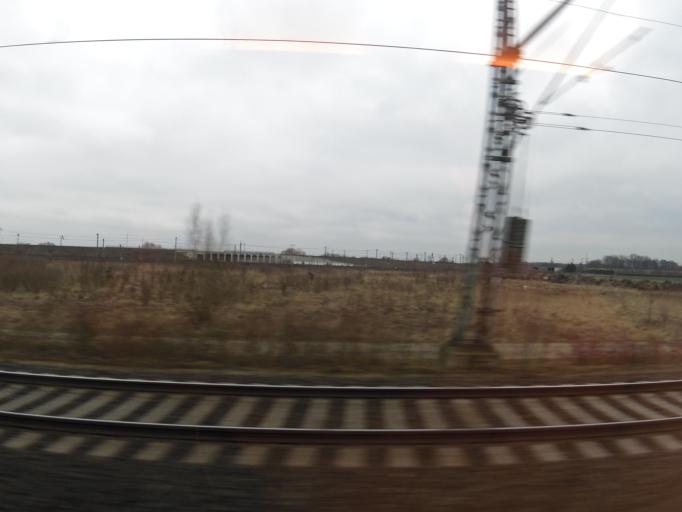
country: DE
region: Lower Saxony
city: Lehrte
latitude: 52.3688
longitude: 10.0020
